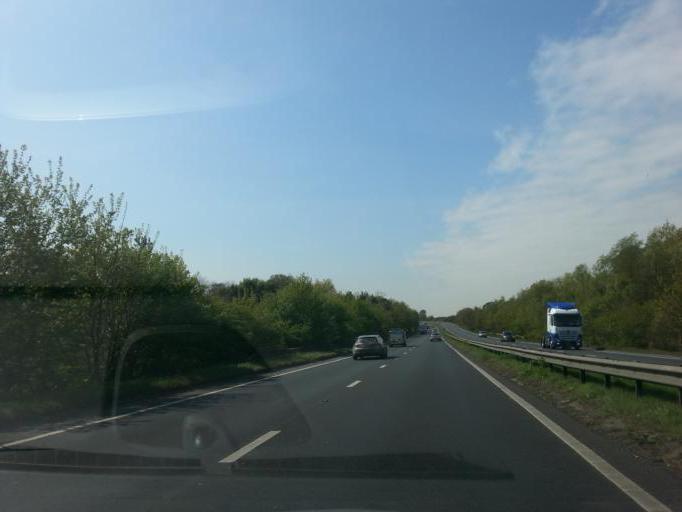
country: GB
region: England
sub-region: Suffolk
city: Kesgrave
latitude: 52.0442
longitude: 1.2688
